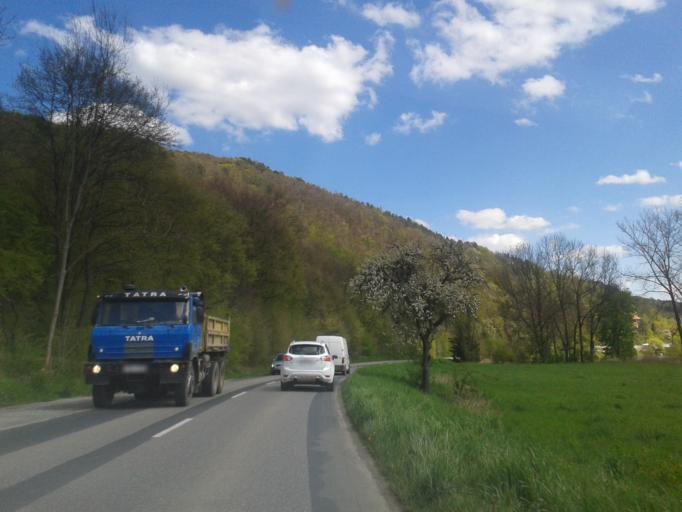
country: CZ
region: Central Bohemia
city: Hyskov
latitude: 49.9901
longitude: 14.0606
